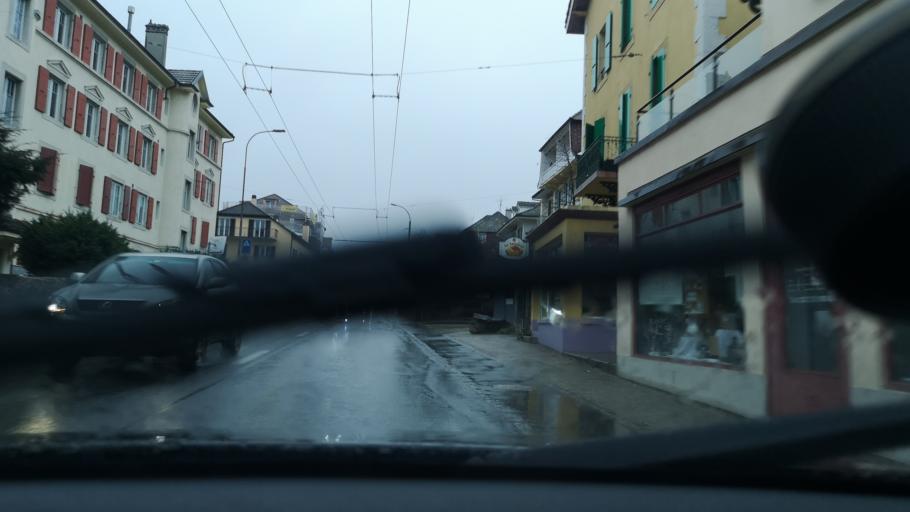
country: CH
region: Neuchatel
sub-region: Boudry District
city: Peseux
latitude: 46.9853
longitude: 6.8827
